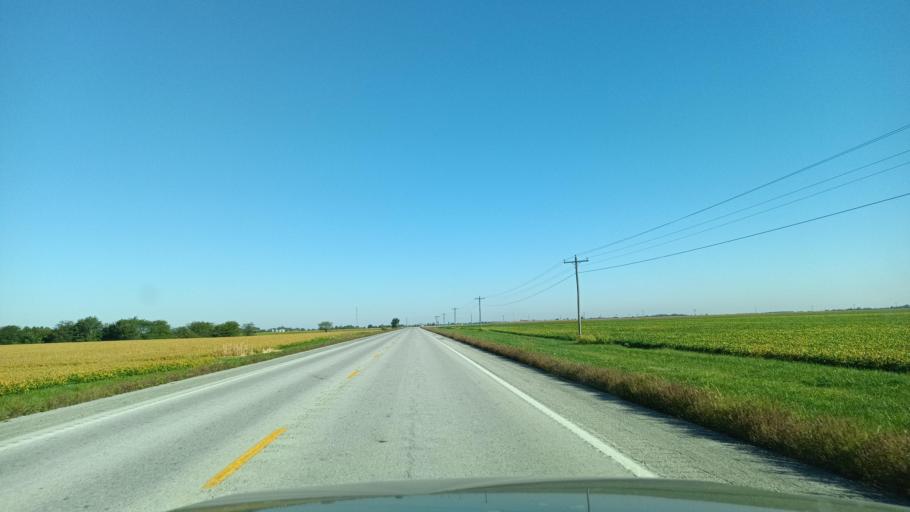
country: US
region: Missouri
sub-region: Audrain County
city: Vandalia
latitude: 39.4047
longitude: -91.6415
